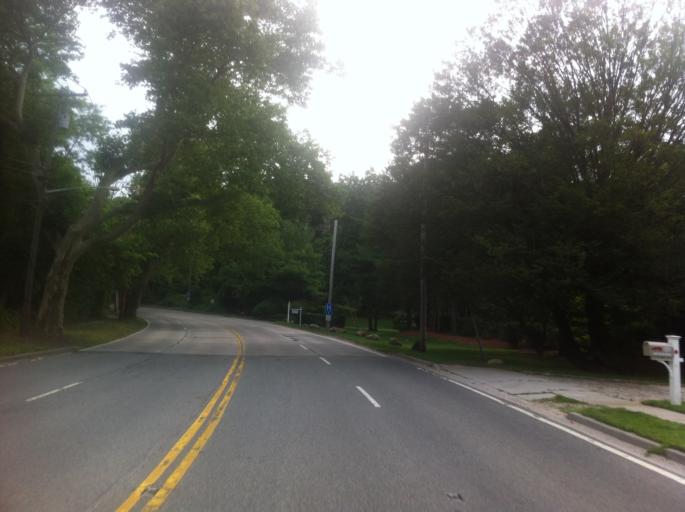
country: US
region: New York
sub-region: Nassau County
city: Lattingtown
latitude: 40.9082
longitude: -73.5837
